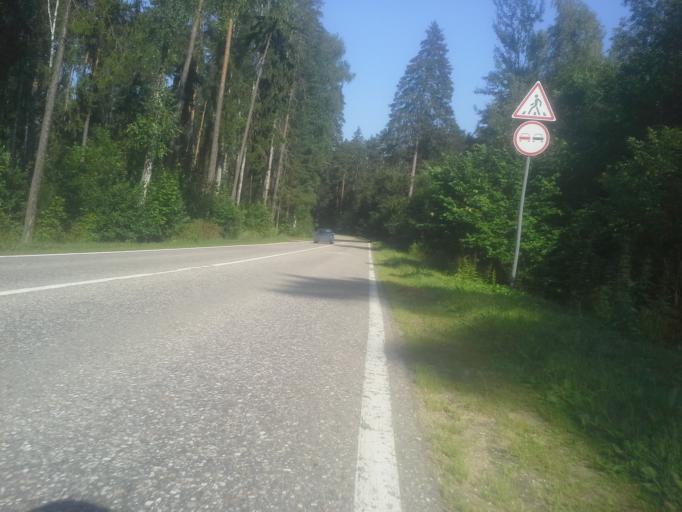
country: RU
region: Moskovskaya
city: Karinskoye
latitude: 55.6962
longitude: 36.7295
